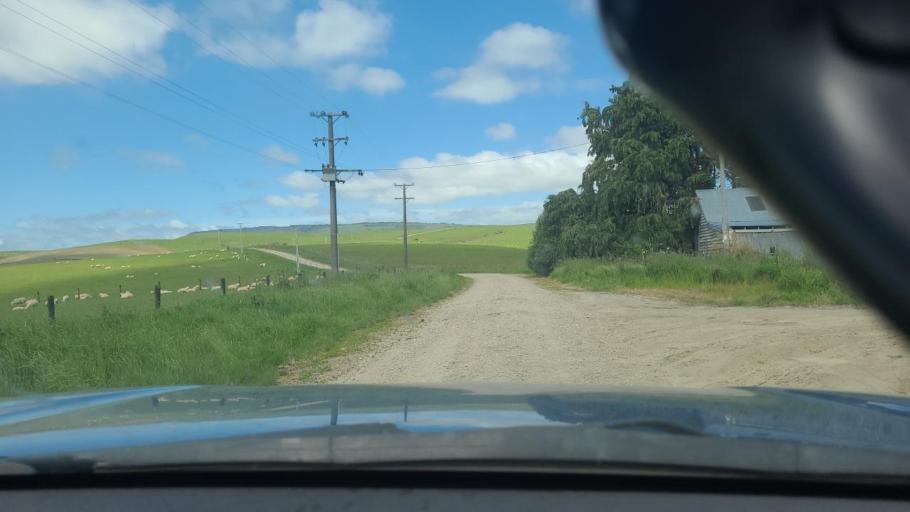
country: NZ
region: Southland
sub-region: Gore District
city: Gore
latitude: -46.3642
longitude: 168.9469
